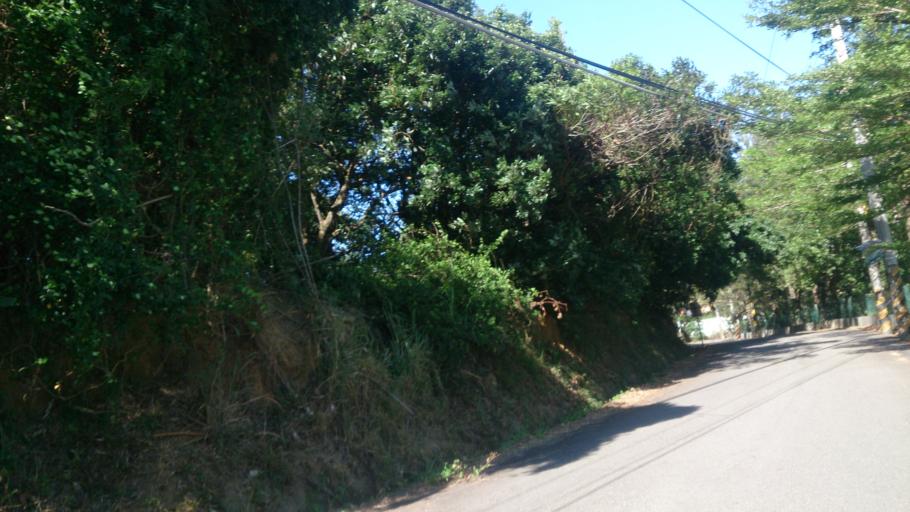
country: TW
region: Taiwan
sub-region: Hsinchu
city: Hsinchu
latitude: 24.7528
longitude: 120.9498
